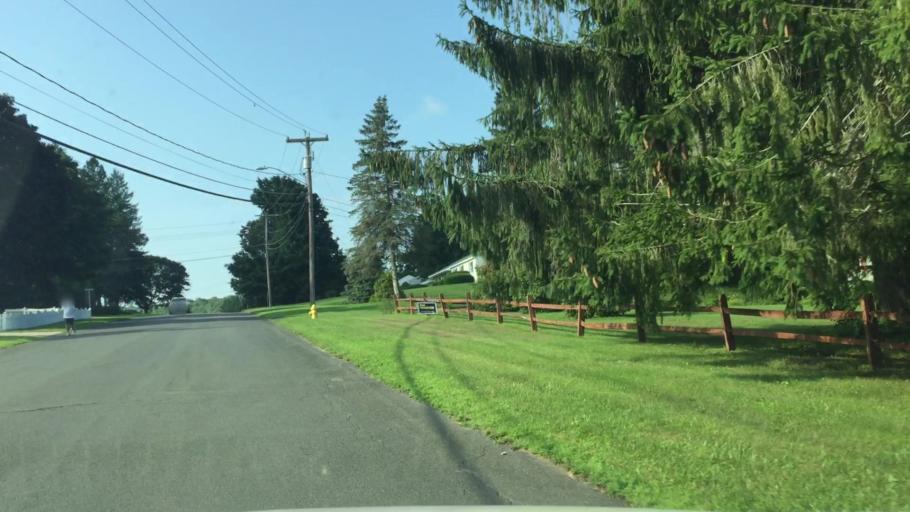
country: US
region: Massachusetts
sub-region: Berkshire County
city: Pittsfield
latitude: 42.4308
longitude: -73.2122
